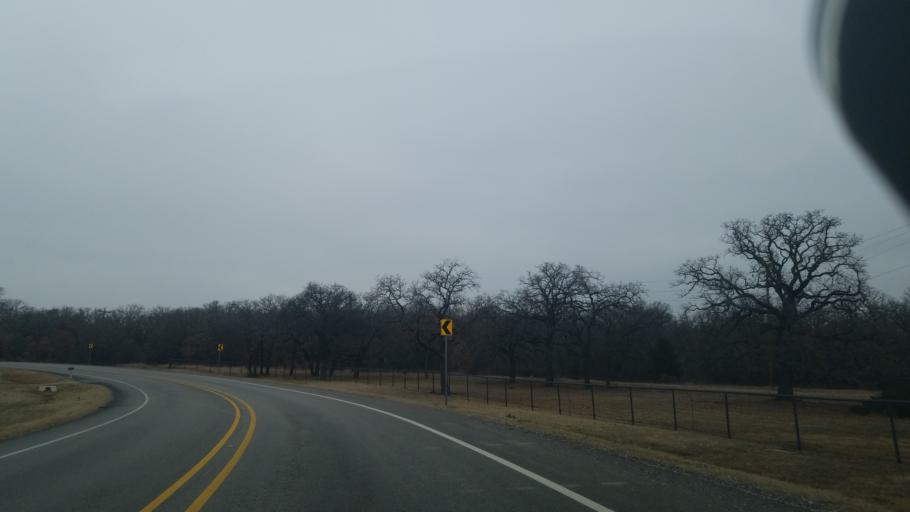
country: US
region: Texas
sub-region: Denton County
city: Argyle
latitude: 33.1285
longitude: -97.1398
